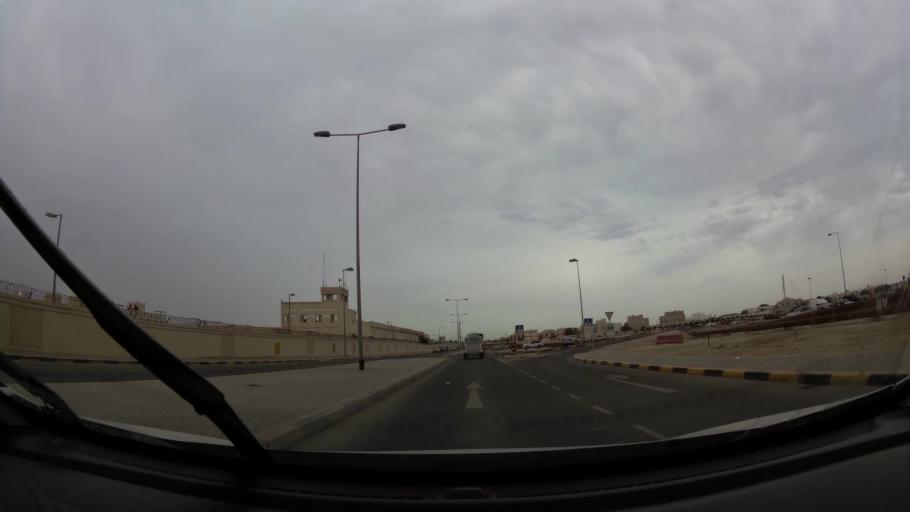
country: BH
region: Central Governorate
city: Madinat Hamad
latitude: 26.1554
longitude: 50.4806
